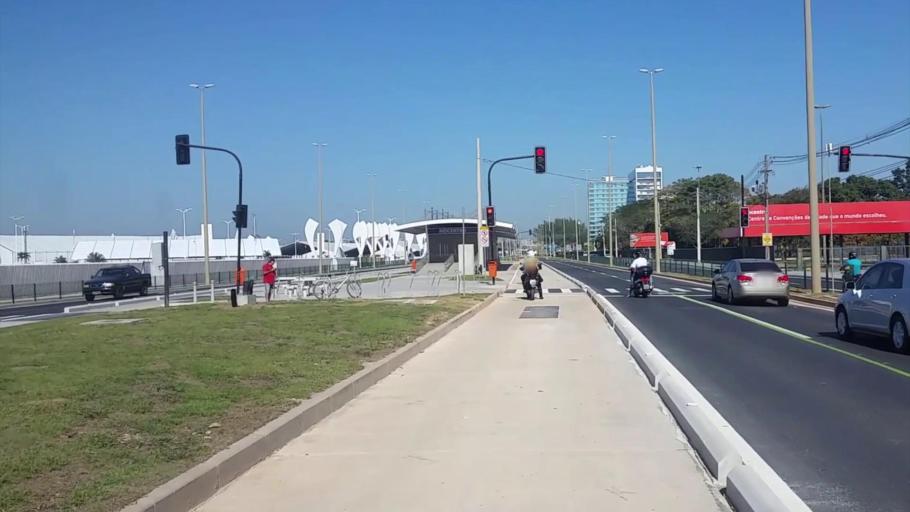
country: BR
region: Rio de Janeiro
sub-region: Nilopolis
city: Nilopolis
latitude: -22.9761
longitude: -43.4058
